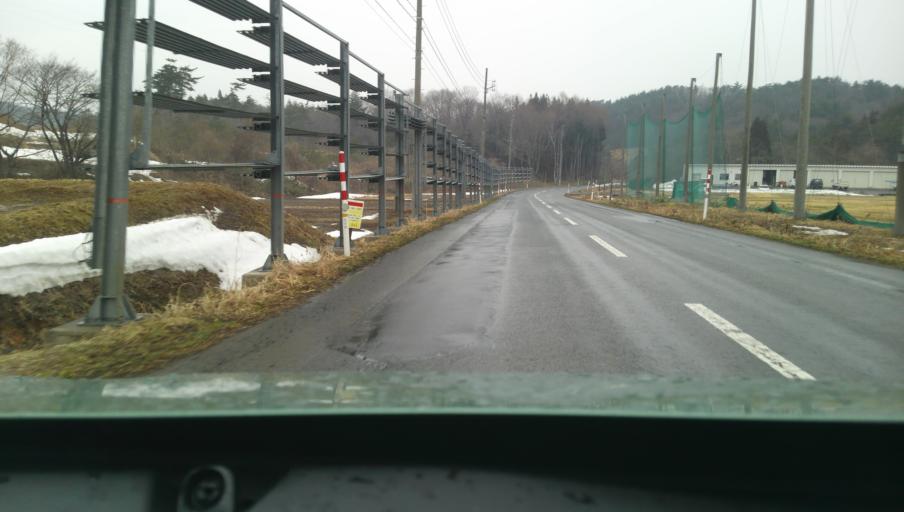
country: JP
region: Iwate
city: Kitakami
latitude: 39.2706
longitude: 140.9808
